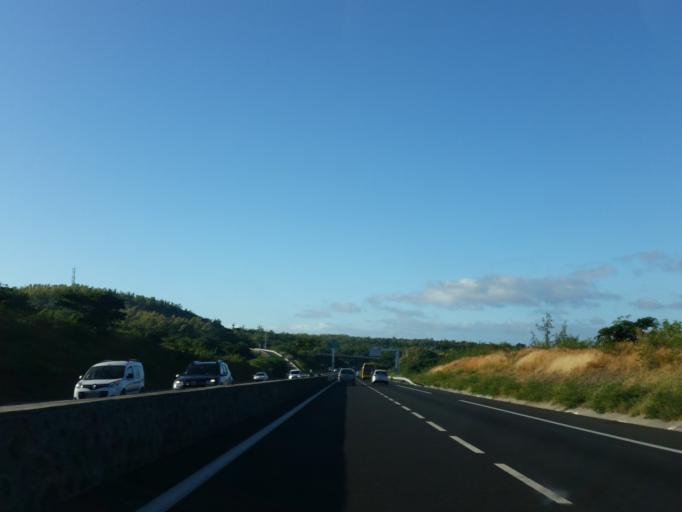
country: RE
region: Reunion
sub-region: Reunion
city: Les Avirons
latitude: -21.2598
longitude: 55.3355
